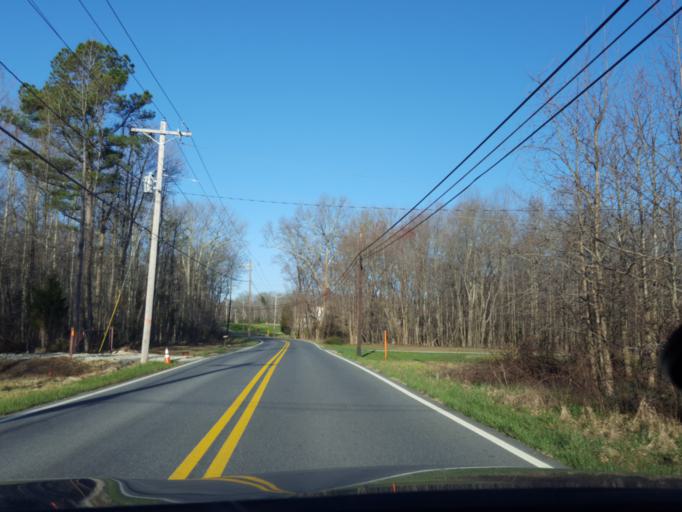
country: US
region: Maryland
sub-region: Prince George's County
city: Brandywine
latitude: 38.6623
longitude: -76.8215
